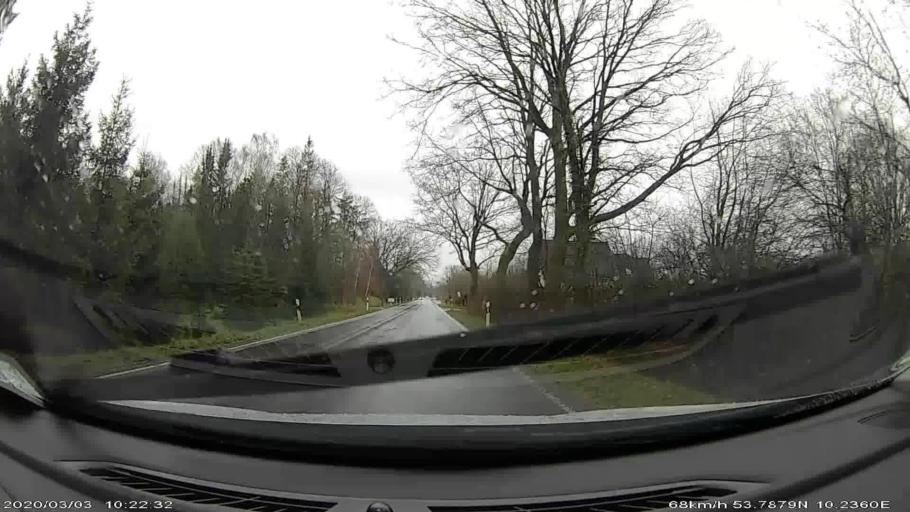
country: DE
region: Schleswig-Holstein
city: Sulfeld
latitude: 53.7851
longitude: 10.2393
